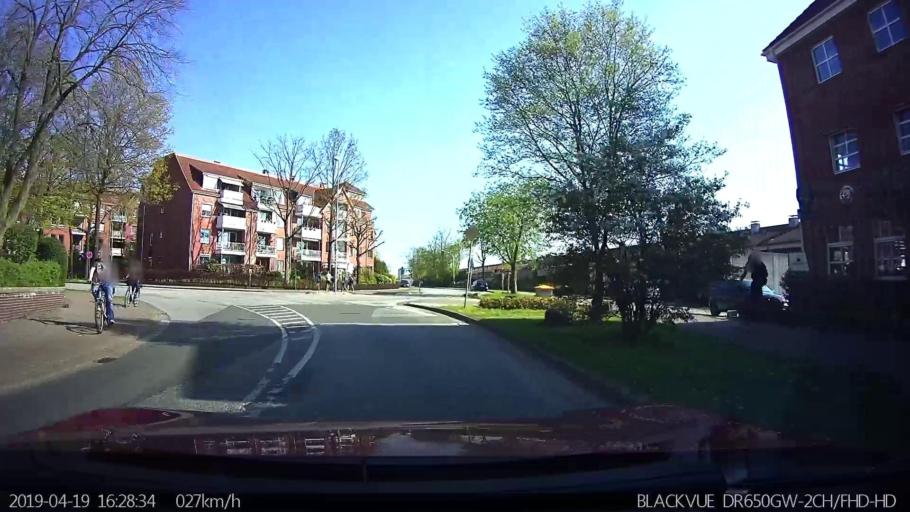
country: DE
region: Schleswig-Holstein
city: Pinneberg
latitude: 53.6583
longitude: 9.7943
